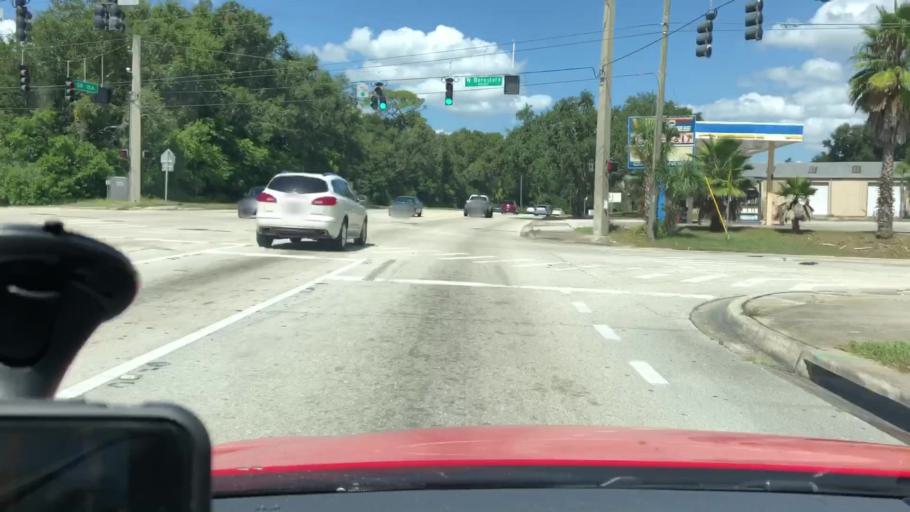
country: US
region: Florida
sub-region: Volusia County
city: West DeLand
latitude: 29.0132
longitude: -81.3232
